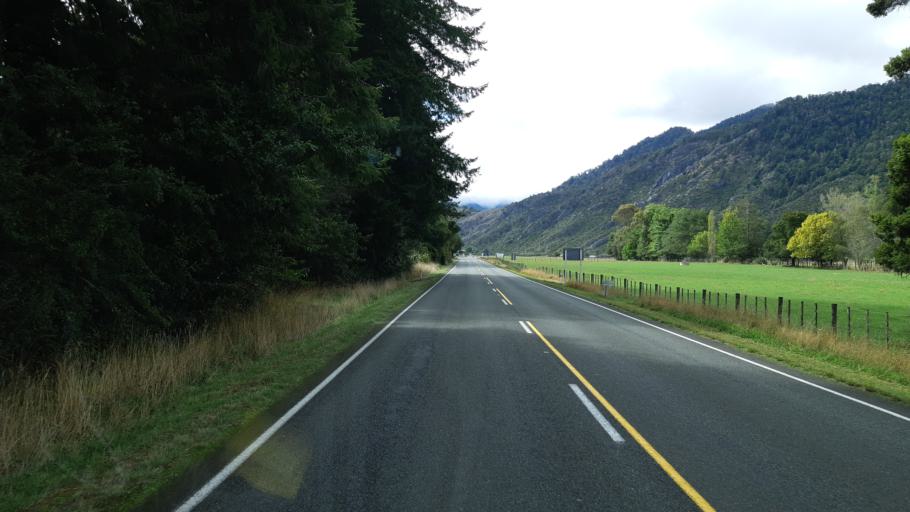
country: NZ
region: West Coast
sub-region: Buller District
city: Westport
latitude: -41.7963
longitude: 172.3422
